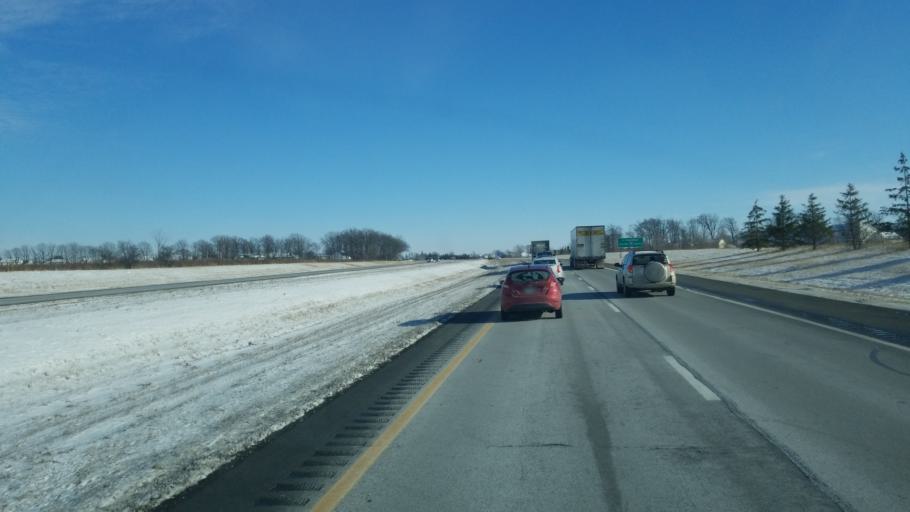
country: US
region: Ohio
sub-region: Lucas County
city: Maumee
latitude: 41.5353
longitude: -83.6713
